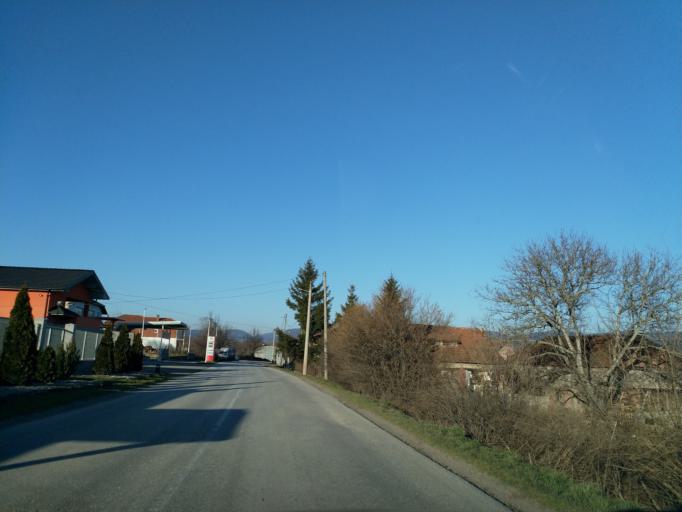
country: RS
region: Central Serbia
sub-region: Pomoravski Okrug
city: Paracin
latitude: 43.8821
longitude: 21.4765
